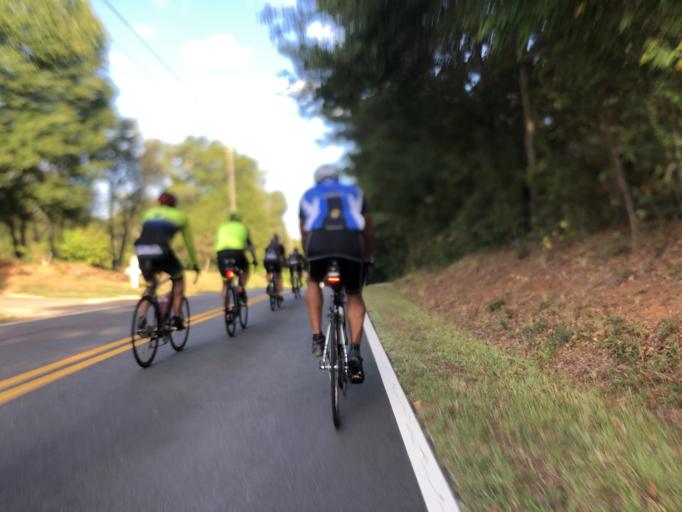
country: US
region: Georgia
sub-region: Fulton County
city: Palmetto
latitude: 33.5811
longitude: -84.6928
